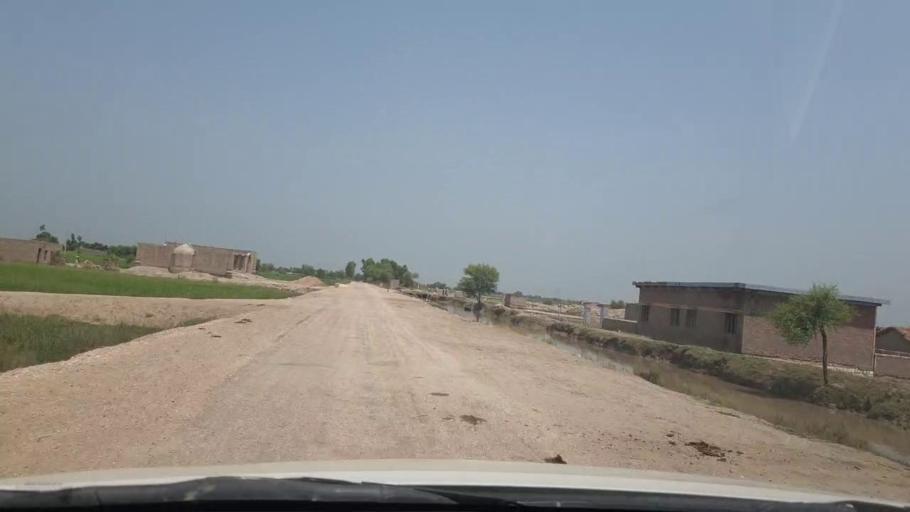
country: PK
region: Sindh
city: Rustam jo Goth
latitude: 28.0296
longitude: 68.7848
